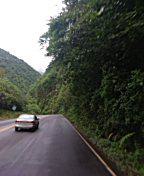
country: CR
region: Heredia
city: Angeles
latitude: 10.0679
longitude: -84.0033
